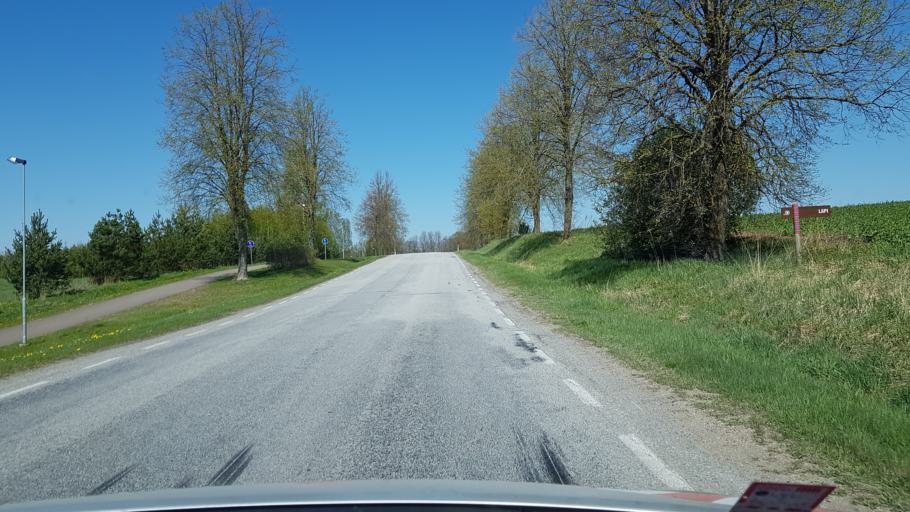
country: EE
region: Vorumaa
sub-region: Voru linn
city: Voru
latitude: 57.8983
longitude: 26.9969
